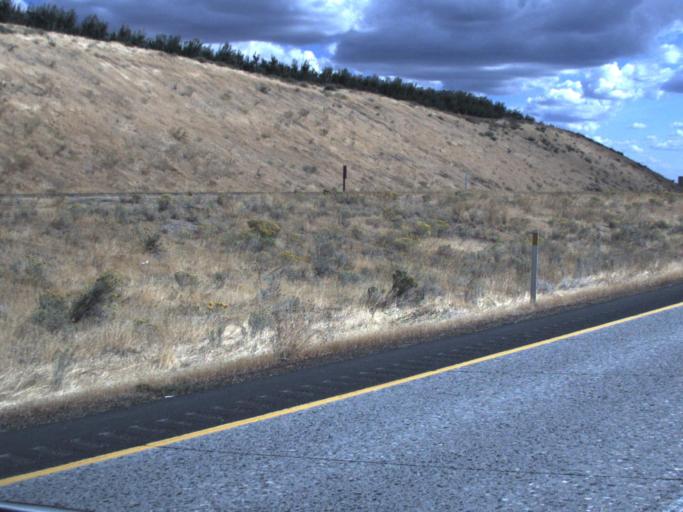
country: US
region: Washington
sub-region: Yakima County
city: Union Gap
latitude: 46.5025
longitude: -120.4482
